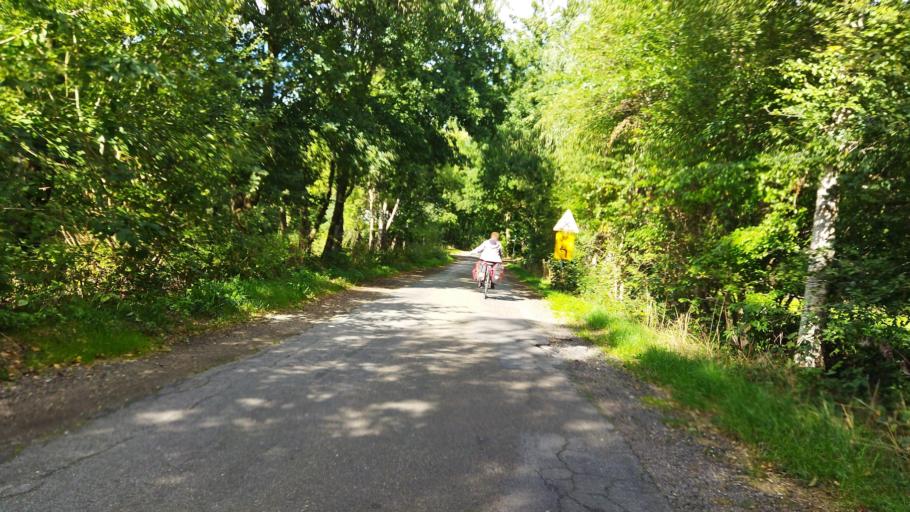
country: DE
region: Lower Saxony
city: Lingen
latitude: 52.4658
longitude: 7.3446
